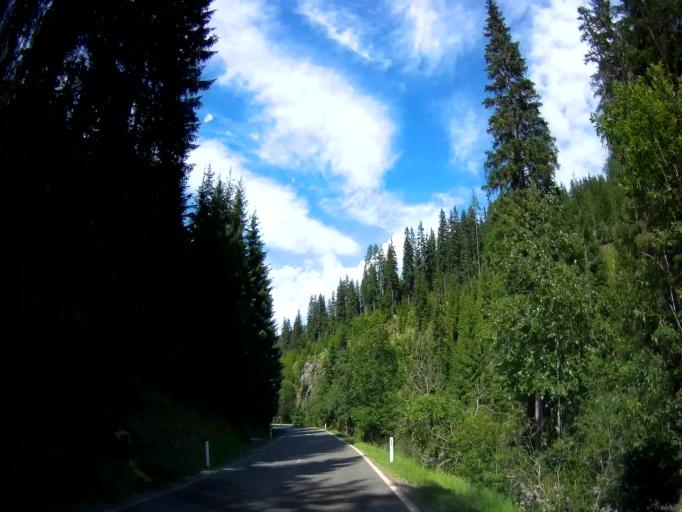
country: AT
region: Styria
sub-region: Politischer Bezirk Murau
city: Stadl an der Mur
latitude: 47.0222
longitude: 14.0059
